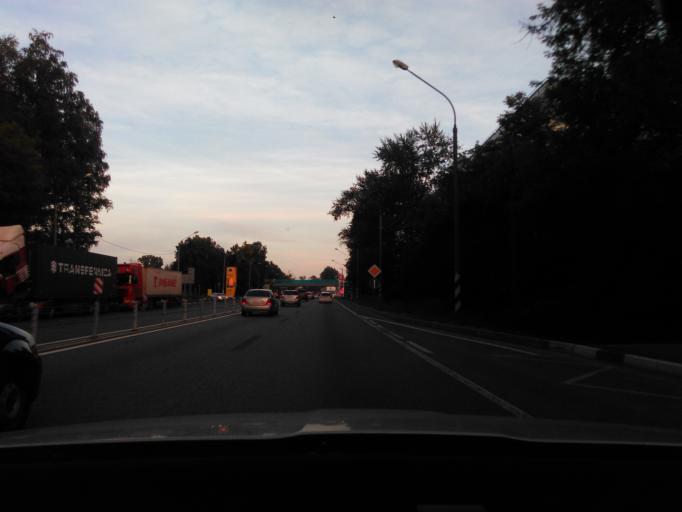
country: RU
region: Moskovskaya
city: Klin
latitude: 56.3391
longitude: 36.7160
